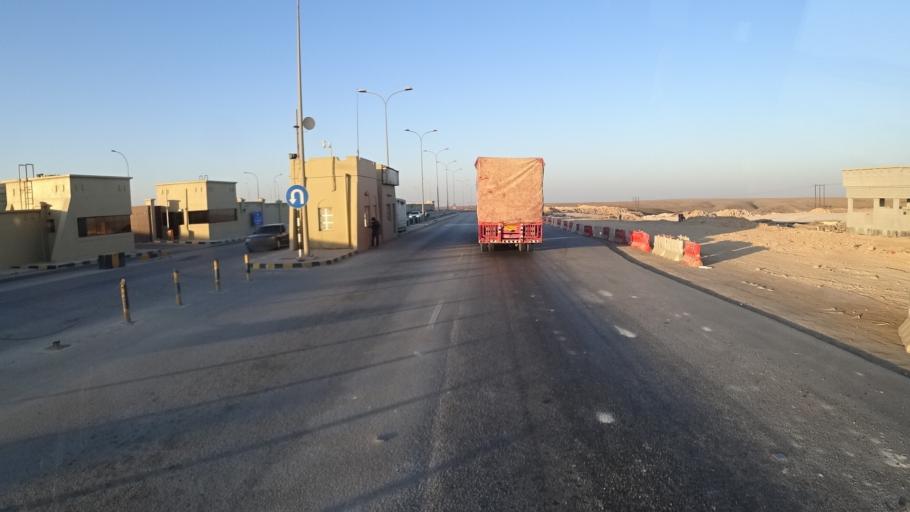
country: OM
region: Zufar
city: Salalah
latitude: 17.2784
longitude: 54.0860
